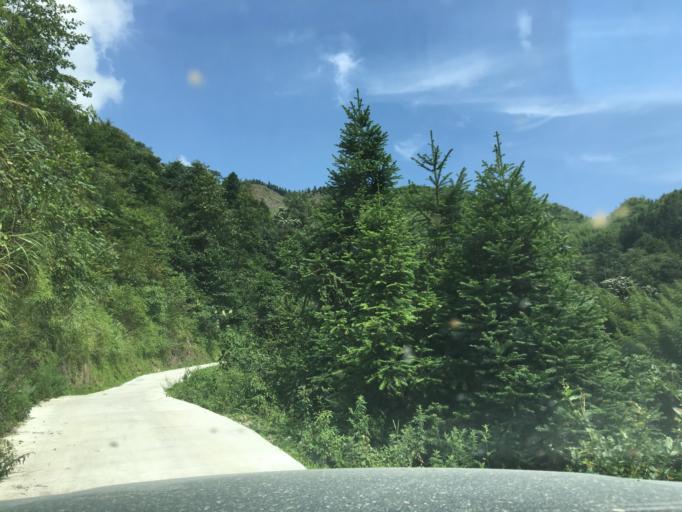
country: CN
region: Guangxi Zhuangzu Zizhiqu
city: Xinzhou
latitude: 24.9702
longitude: 105.6219
